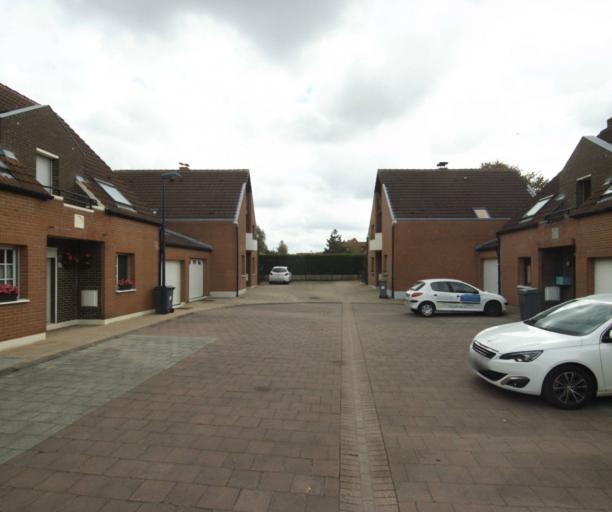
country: FR
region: Nord-Pas-de-Calais
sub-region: Departement du Nord
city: Perenchies
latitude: 50.6629
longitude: 2.9658
